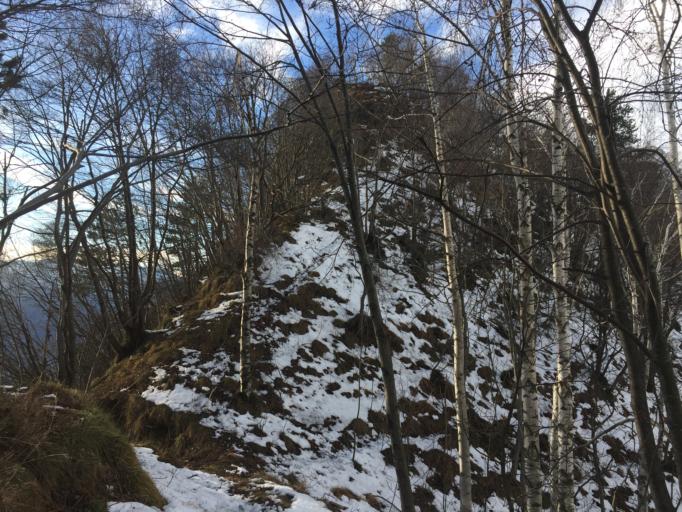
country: IT
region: Friuli Venezia Giulia
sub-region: Provincia di Udine
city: Venzone
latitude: 46.3256
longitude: 13.1526
